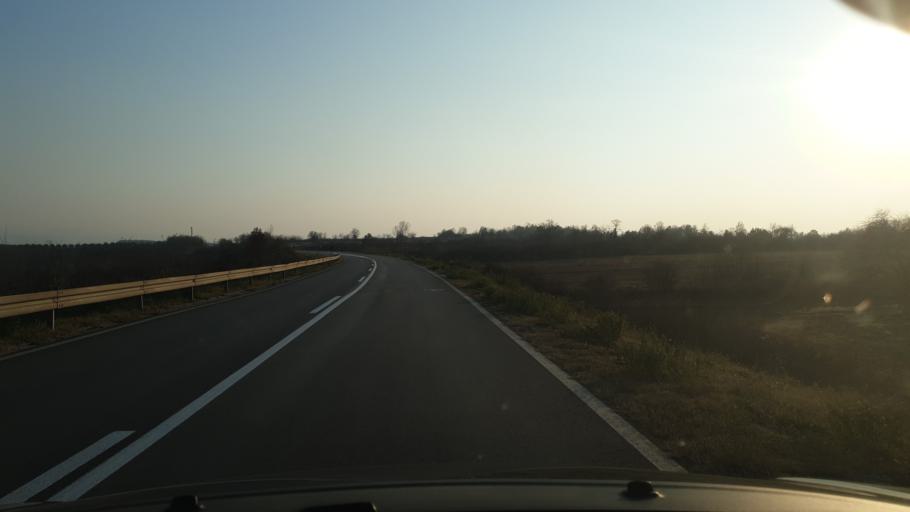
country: RS
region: Central Serbia
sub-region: Zajecarski Okrug
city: Zajecar
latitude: 44.0029
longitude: 22.3018
